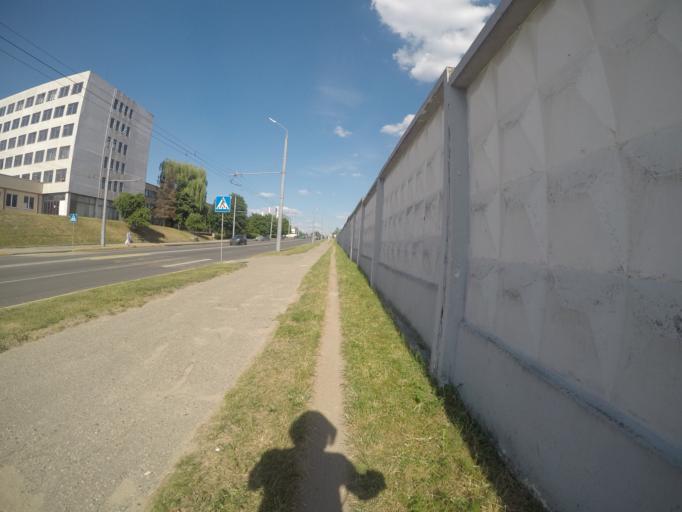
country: BY
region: Grodnenskaya
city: Hrodna
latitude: 53.7056
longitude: 23.8233
